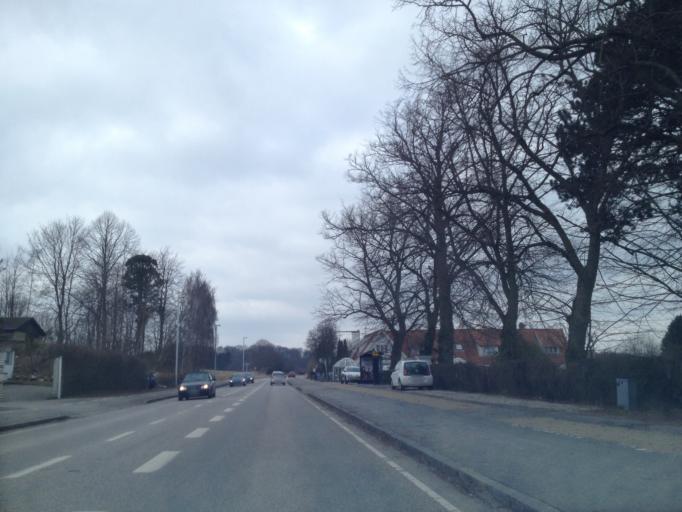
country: DK
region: Capital Region
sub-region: Fredensborg Kommune
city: Kokkedal
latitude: 55.9150
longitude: 12.5178
